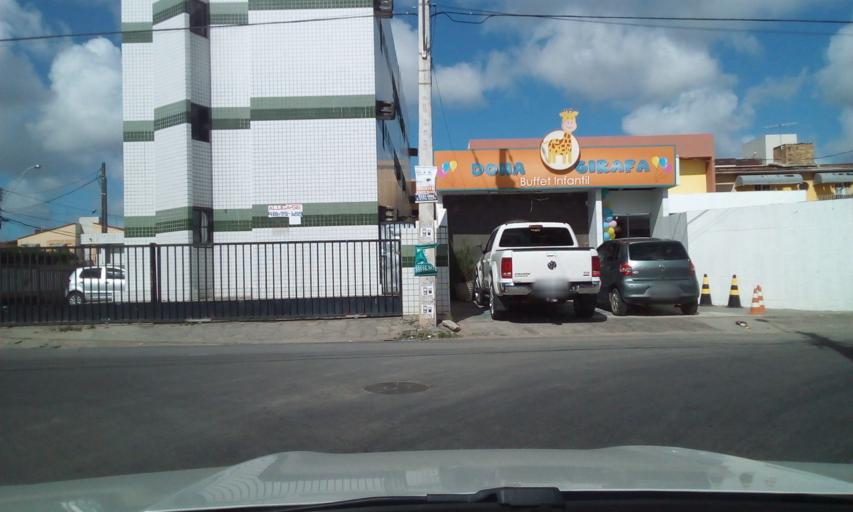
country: BR
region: Paraiba
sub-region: Joao Pessoa
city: Joao Pessoa
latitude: -7.1743
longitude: -34.8601
